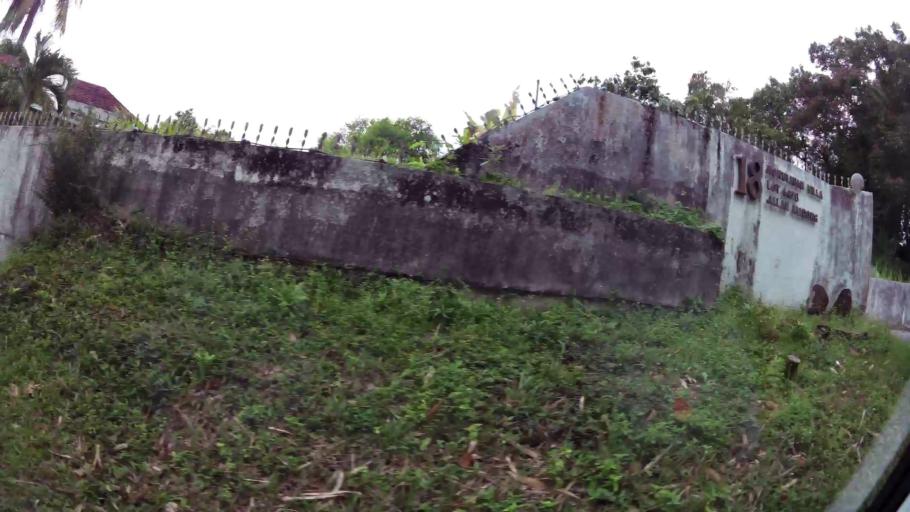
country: BN
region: Brunei and Muara
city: Bandar Seri Begawan
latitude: 4.8926
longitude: 114.9197
